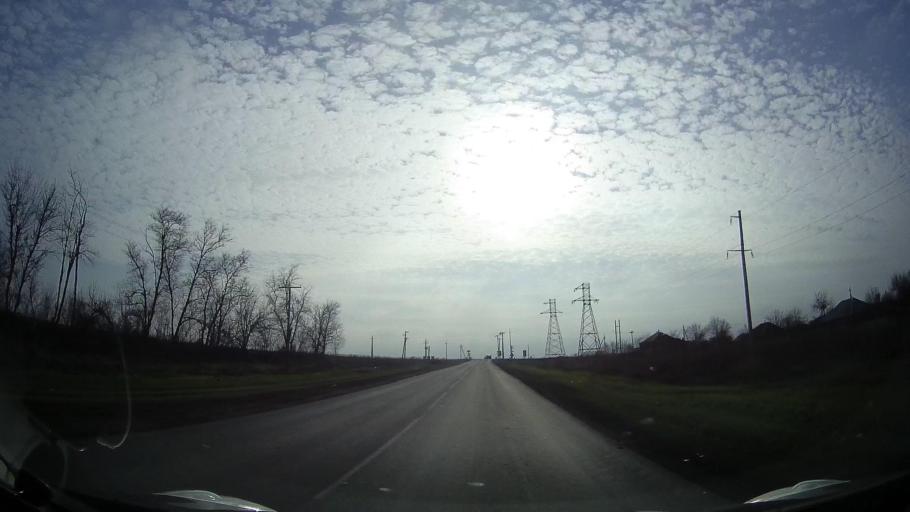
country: RU
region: Rostov
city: Mechetinskaya
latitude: 46.7925
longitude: 40.4960
